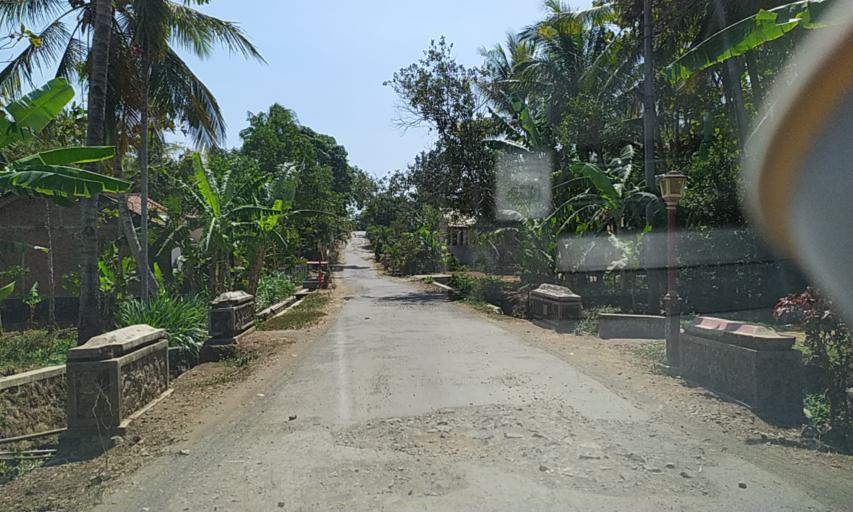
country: ID
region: Central Java
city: Prapagan
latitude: -7.5933
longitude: 108.9924
